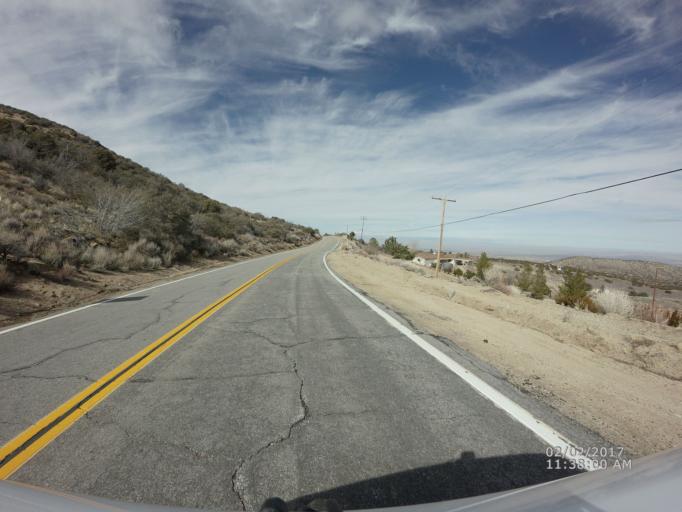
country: US
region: California
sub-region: Los Angeles County
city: Littlerock
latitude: 34.4283
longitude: -117.9186
